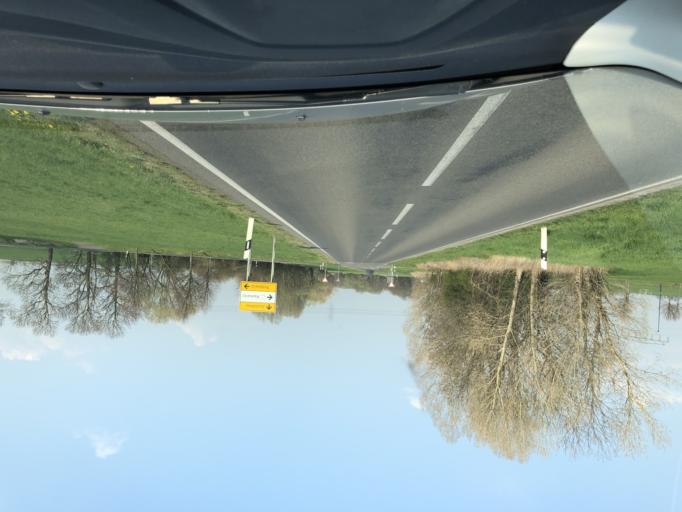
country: DE
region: Saxony
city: Rackwitz
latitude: 51.4350
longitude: 12.3864
